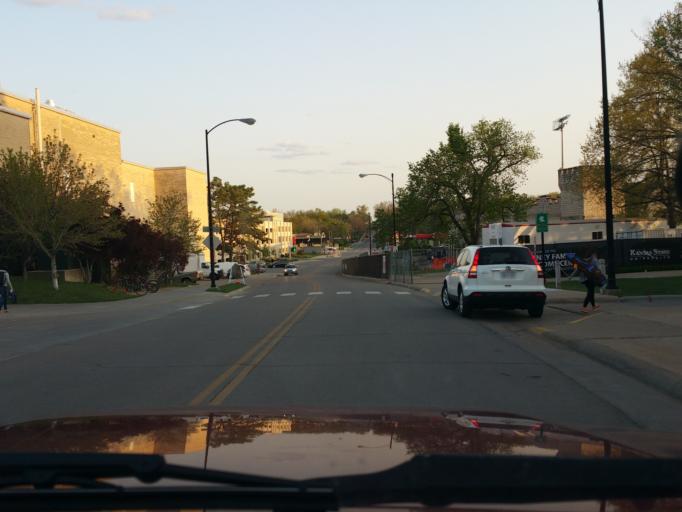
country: US
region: Kansas
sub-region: Riley County
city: Manhattan
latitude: 39.1889
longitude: -96.5833
